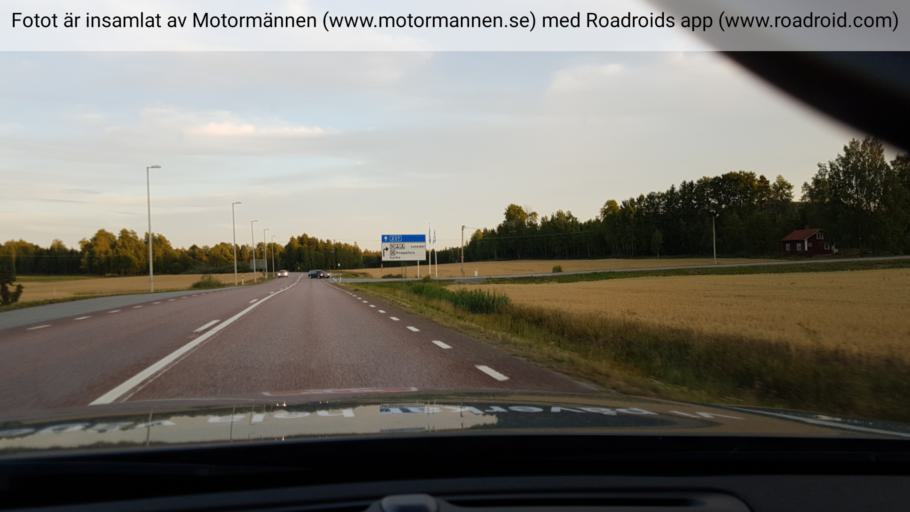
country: SE
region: OErebro
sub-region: Karlskoga Kommun
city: Karlskoga
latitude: 59.4048
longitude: 14.4310
